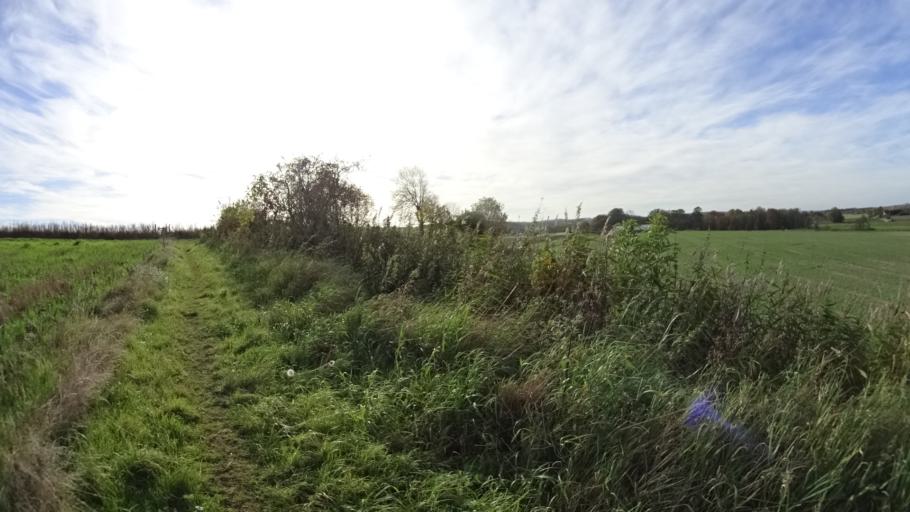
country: DK
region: Central Jutland
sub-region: Arhus Kommune
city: Framlev
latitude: 56.1293
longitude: 10.0204
